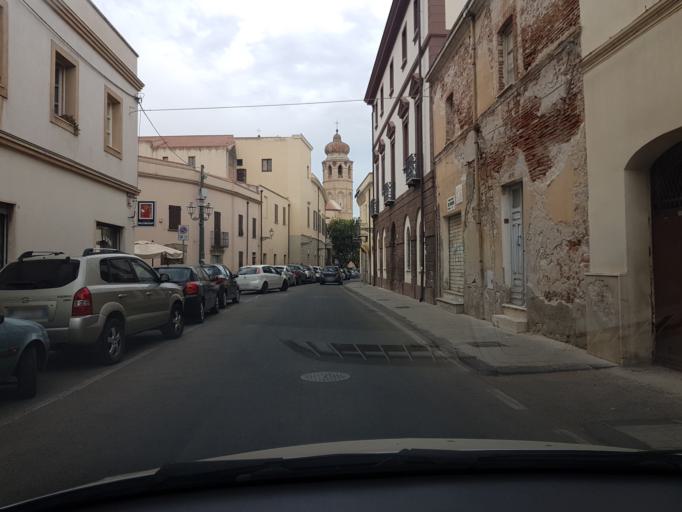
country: IT
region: Sardinia
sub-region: Provincia di Oristano
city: Oristano
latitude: 39.9021
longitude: 8.5919
